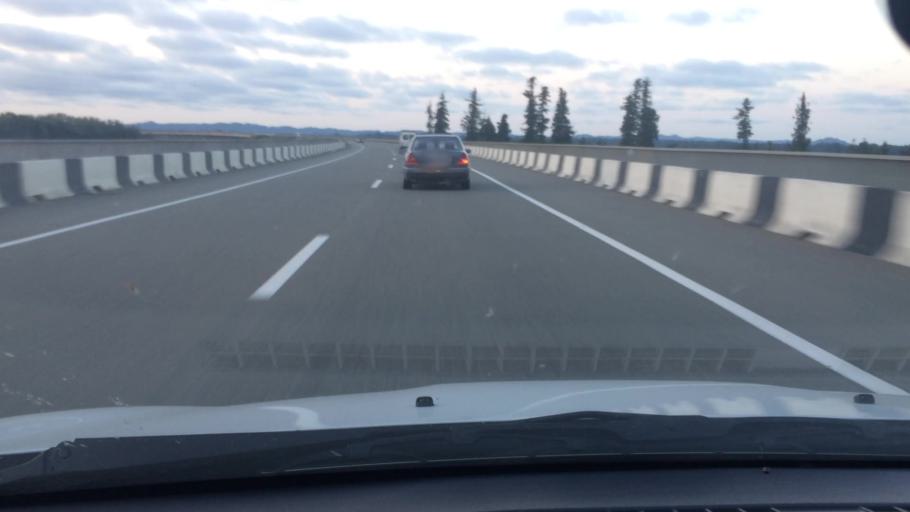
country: GE
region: Ajaria
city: Ochkhamuri
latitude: 41.8597
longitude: 41.8382
